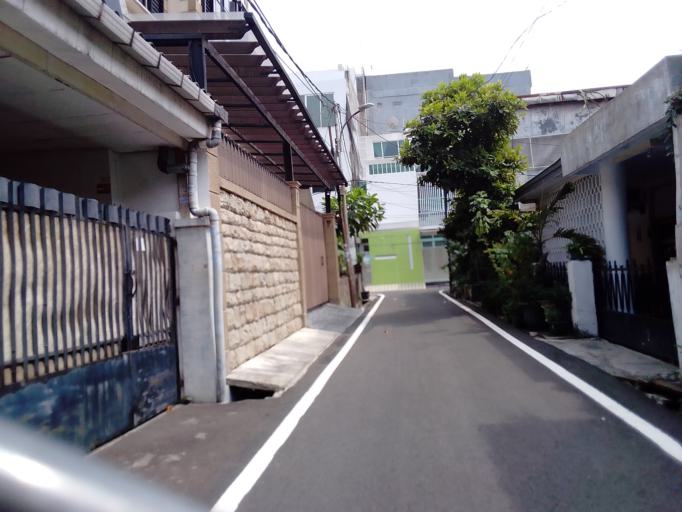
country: ID
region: Jakarta Raya
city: Jakarta
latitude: -6.1750
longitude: 106.8105
